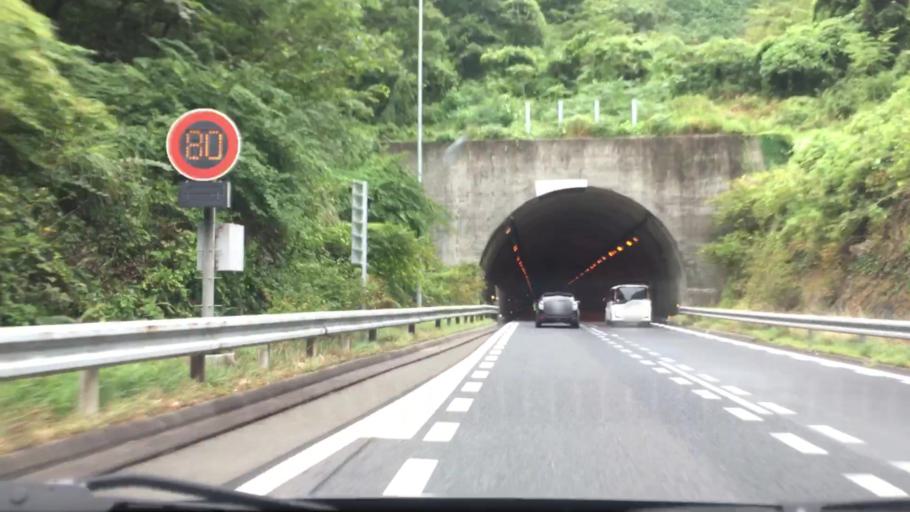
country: JP
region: Okayama
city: Tsuyama
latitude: 35.0149
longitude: 134.2677
